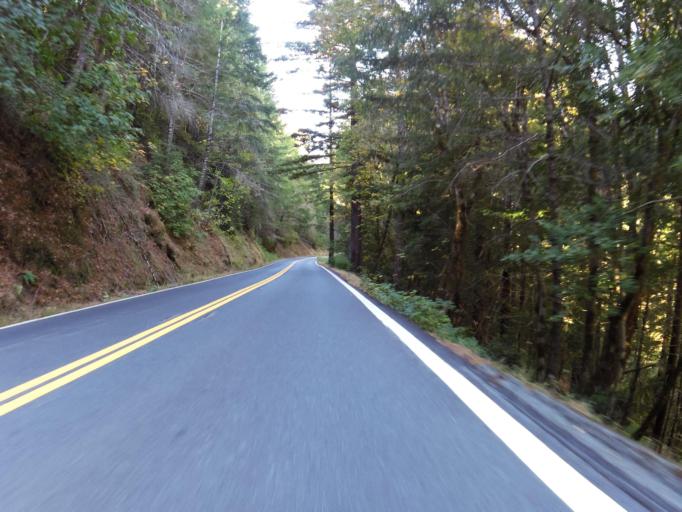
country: US
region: California
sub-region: Humboldt County
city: Redway
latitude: 39.8656
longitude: -123.7196
